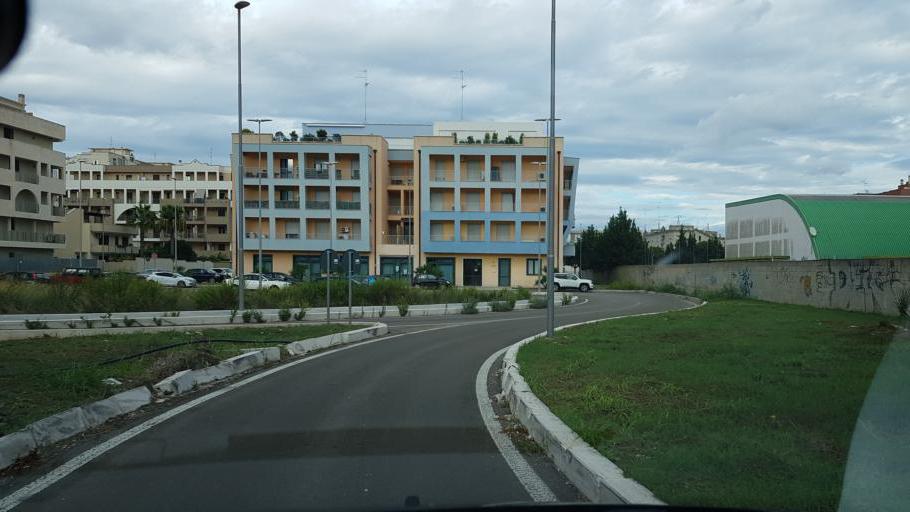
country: IT
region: Apulia
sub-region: Provincia di Lecce
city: Lecce
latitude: 40.3452
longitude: 18.1842
